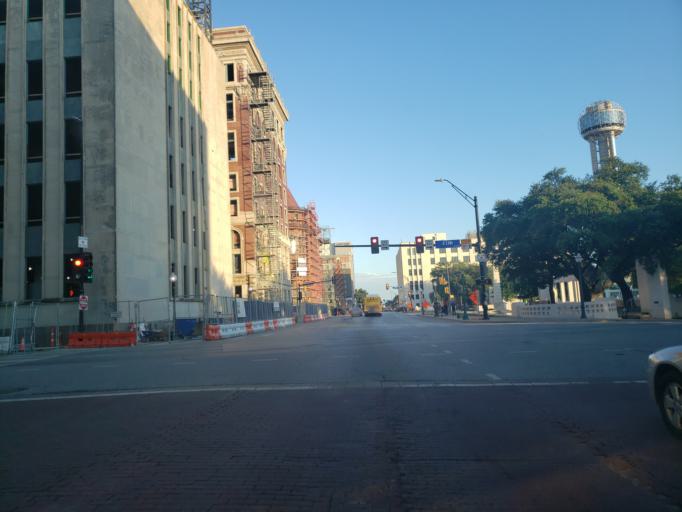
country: US
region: Texas
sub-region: Dallas County
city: Dallas
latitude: 32.7798
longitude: -96.8082
